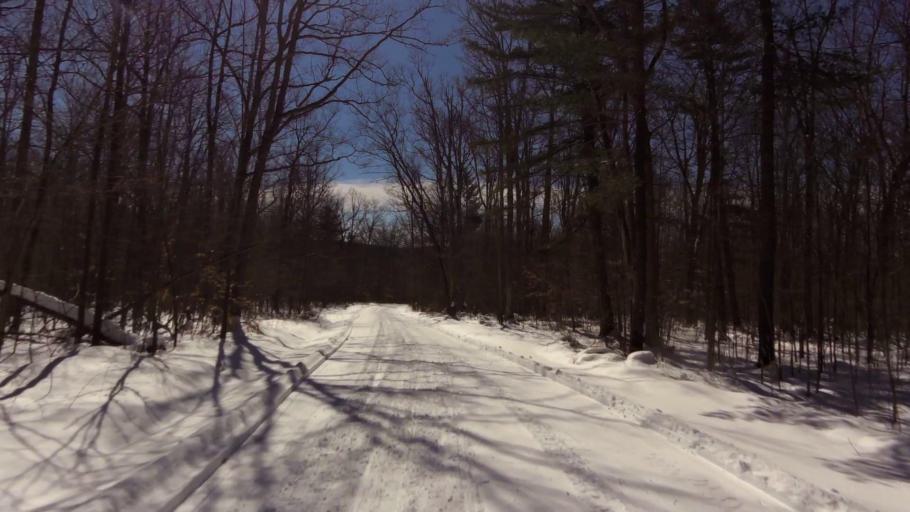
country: US
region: New York
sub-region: Allegany County
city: Houghton
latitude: 42.3359
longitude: -78.2048
